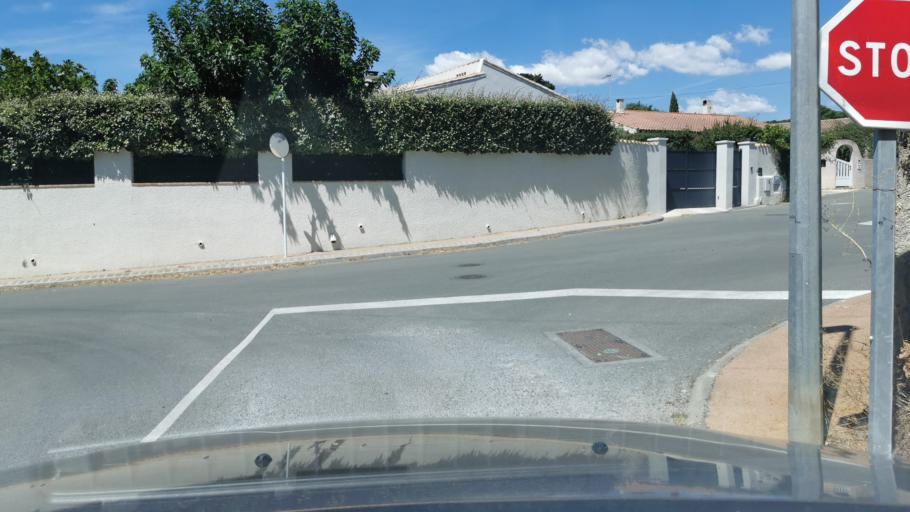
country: FR
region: Languedoc-Roussillon
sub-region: Departement de l'Aude
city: Armissan
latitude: 43.1885
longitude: 3.0980
